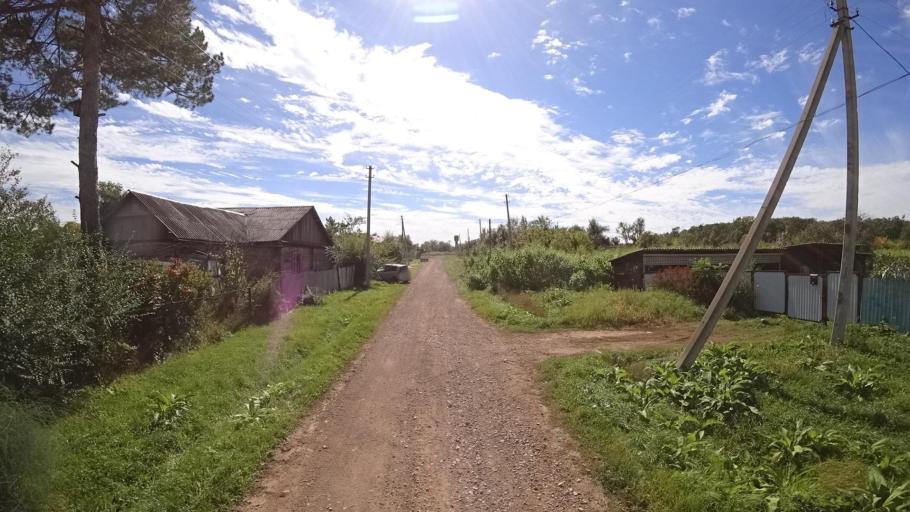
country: RU
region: Primorskiy
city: Yakovlevka
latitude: 44.4304
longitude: 133.5612
